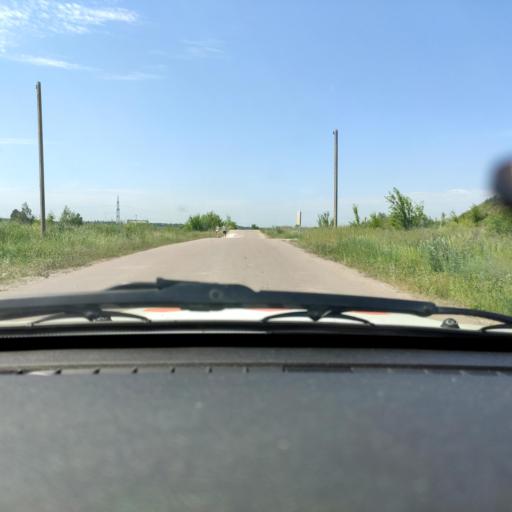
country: RU
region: Voronezj
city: Devitsa
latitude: 51.6245
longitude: 38.9537
